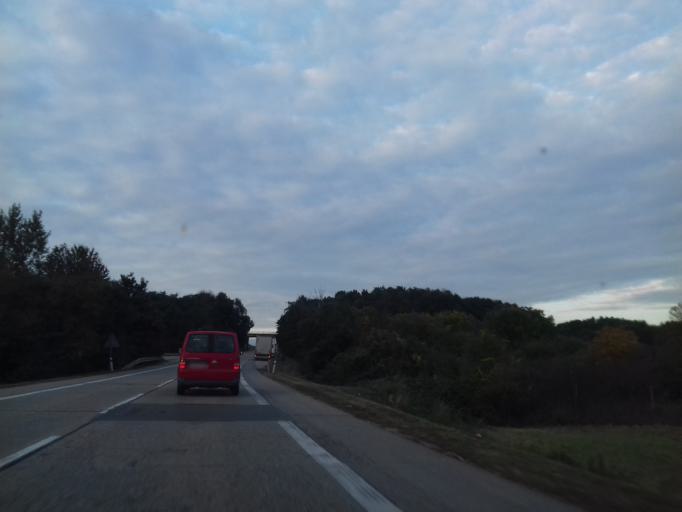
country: SK
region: Trenciansky
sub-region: Okres Trencin
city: Trencin
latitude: 48.8720
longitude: 17.9564
